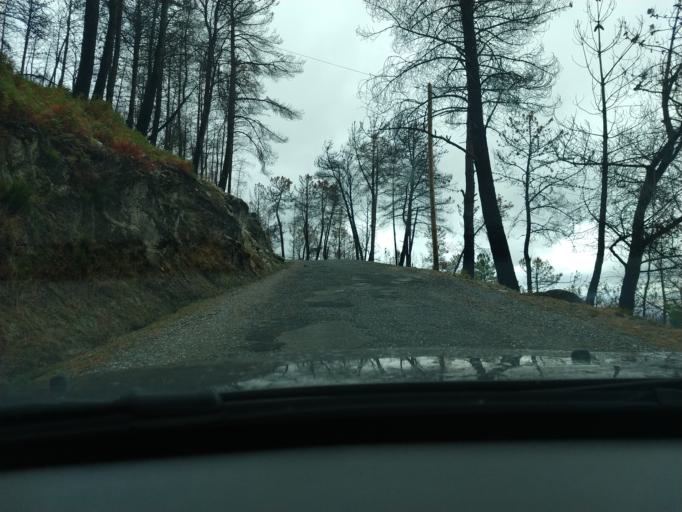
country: PT
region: Guarda
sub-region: Seia
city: Seia
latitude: 40.4189
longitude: -7.6734
